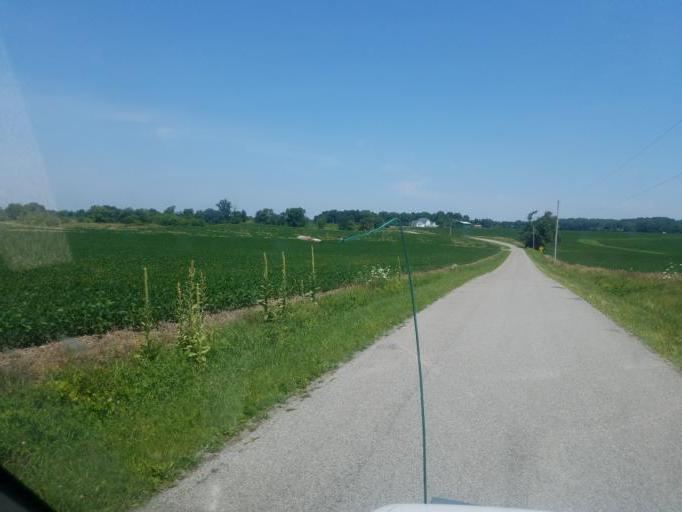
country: US
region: Ohio
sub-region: Logan County
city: West Liberty
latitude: 40.2762
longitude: -83.7665
